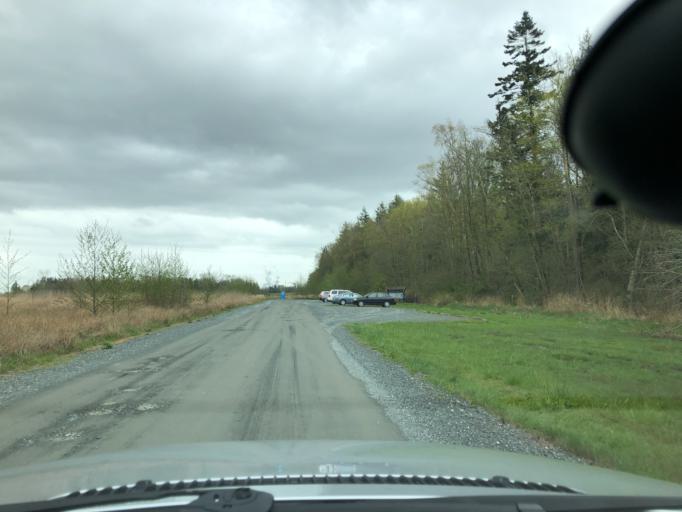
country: US
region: Washington
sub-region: Whatcom County
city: Birch Bay
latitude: 48.8874
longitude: -122.7812
